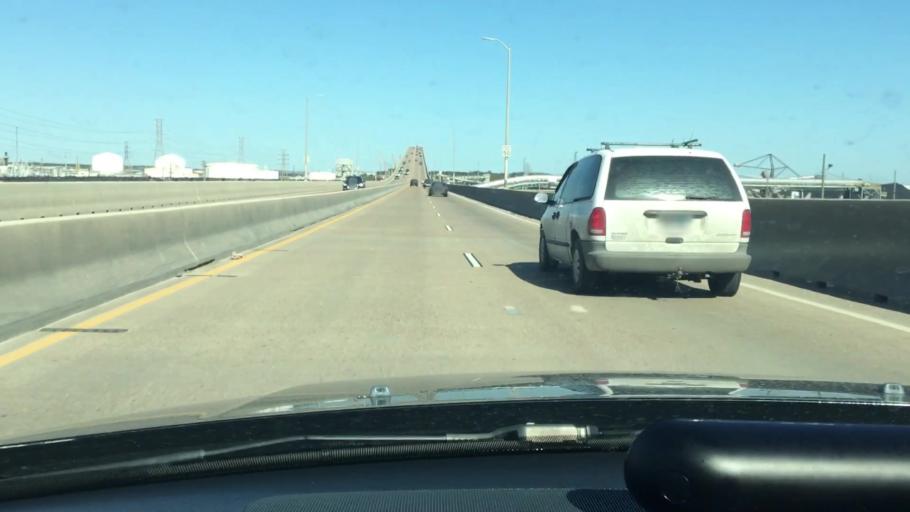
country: US
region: Texas
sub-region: Harris County
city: Deer Park
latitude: 29.7228
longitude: -95.1477
